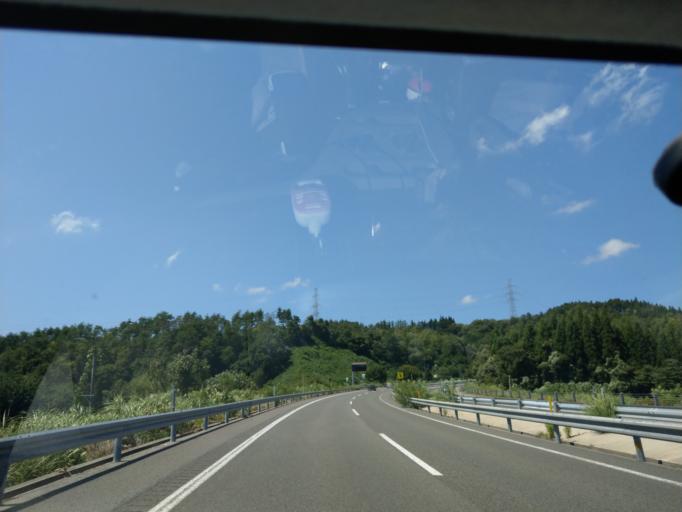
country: JP
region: Akita
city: Omagari
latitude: 39.5710
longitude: 140.3008
